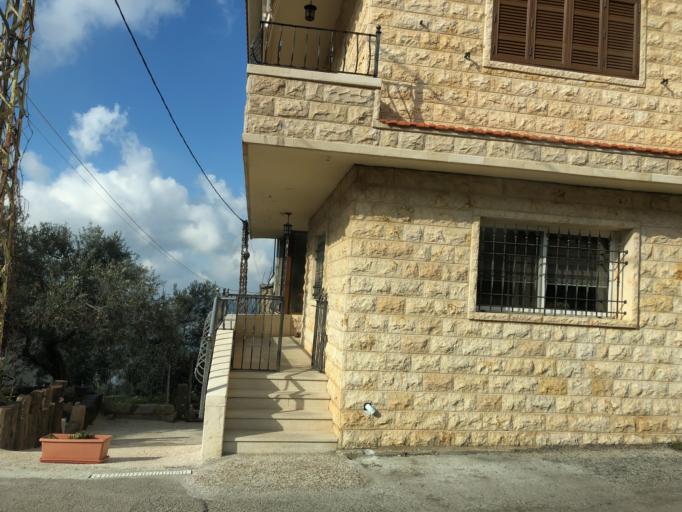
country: LB
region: Liban-Nord
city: Amioun
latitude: 34.2065
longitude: 35.8414
